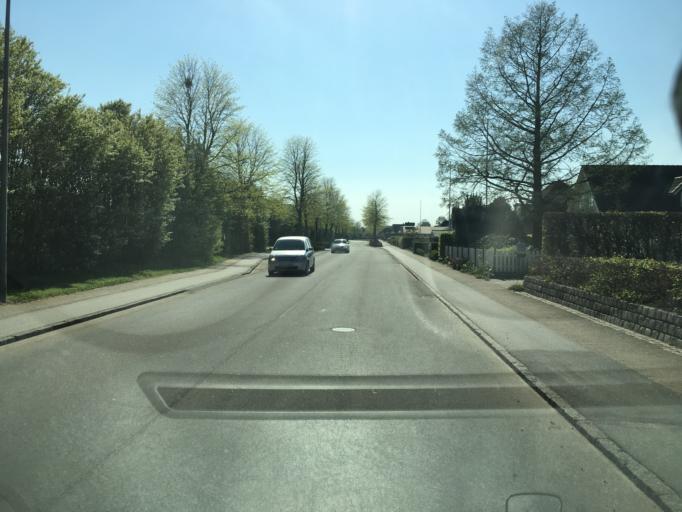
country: DK
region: South Denmark
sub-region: Haderslev Kommune
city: Vojens
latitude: 55.3187
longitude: 9.2985
